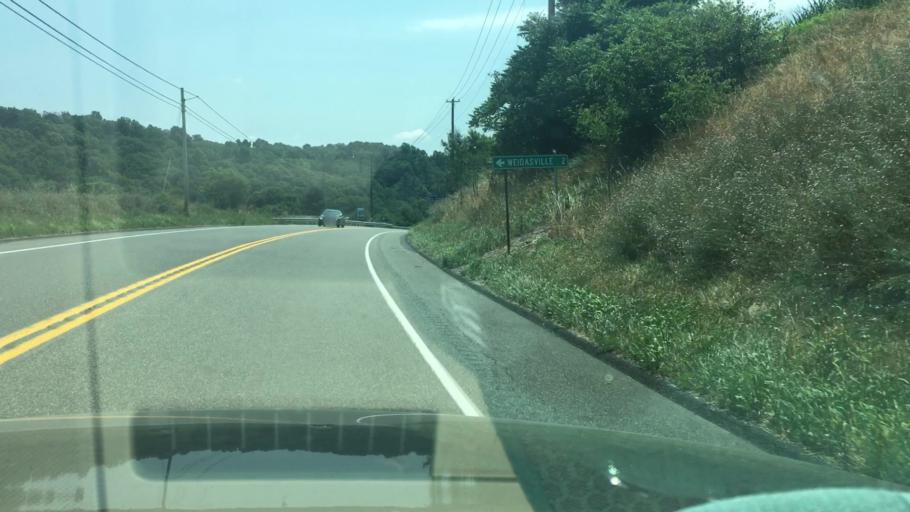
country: US
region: Pennsylvania
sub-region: Lehigh County
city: Schnecksville
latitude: 40.6337
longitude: -75.6736
